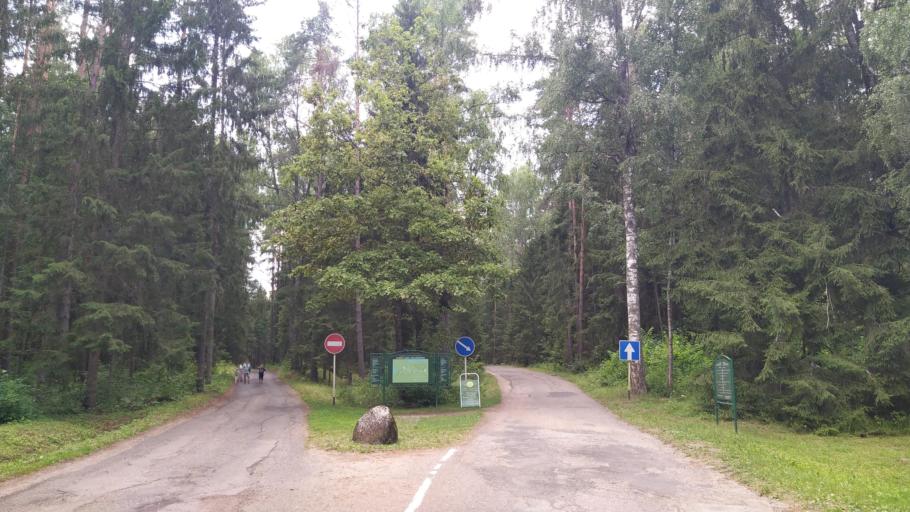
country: RU
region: Pskov
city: Pushkinskiye Gory
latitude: 57.0574
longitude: 28.9443
